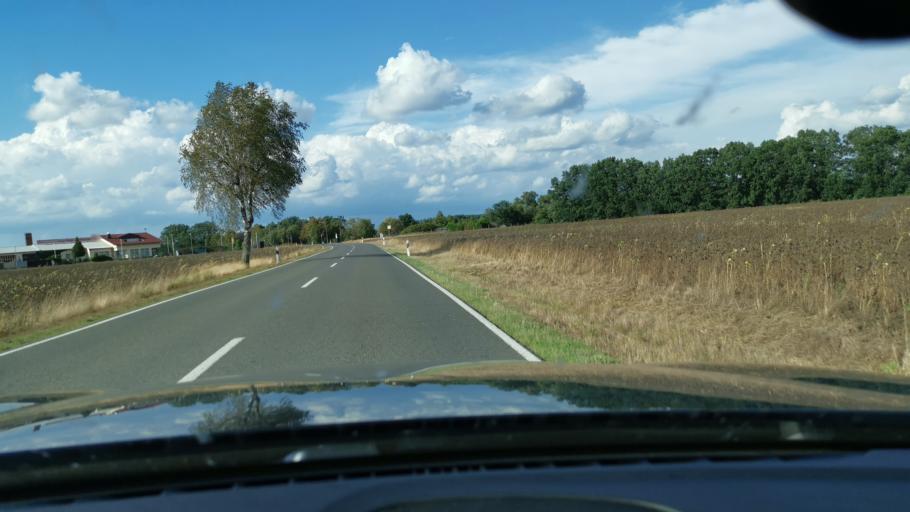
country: DE
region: Saxony
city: Bad Duben
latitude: 51.5461
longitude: 12.5790
